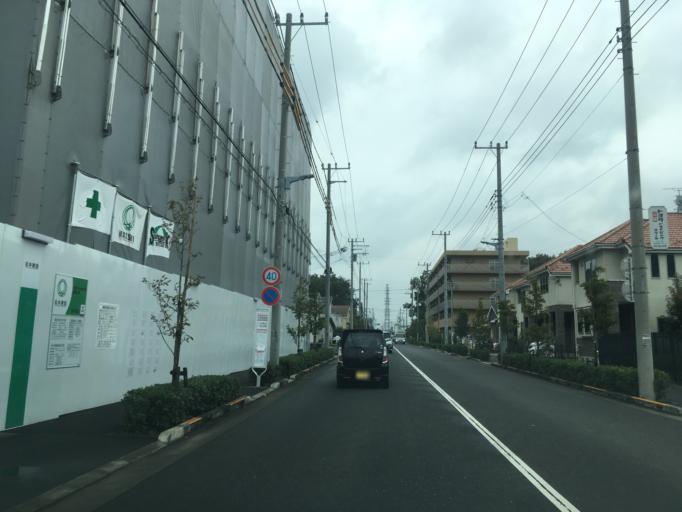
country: JP
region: Tokyo
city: Higashimurayama-shi
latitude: 35.7264
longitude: 139.4434
